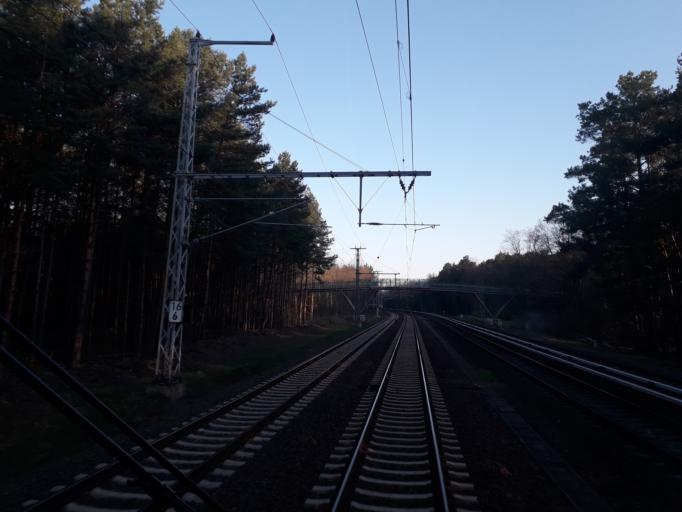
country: DE
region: Berlin
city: Bohnsdorf
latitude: 52.3916
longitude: 13.6021
